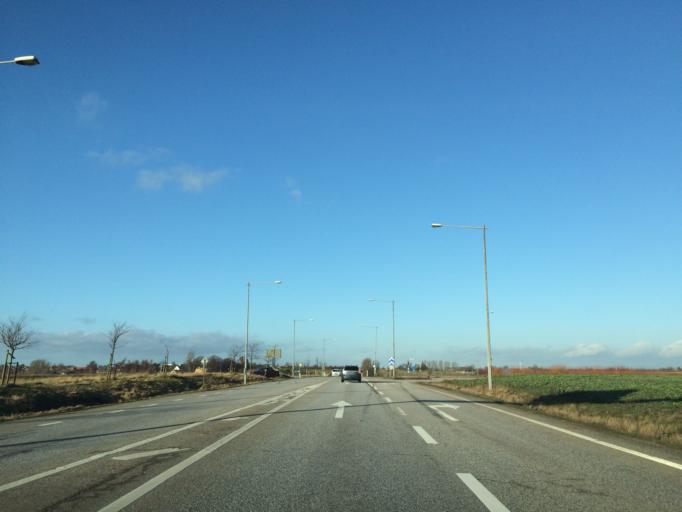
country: SE
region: Skane
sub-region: Kavlinge Kommun
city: Loddekopinge
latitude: 55.7481
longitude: 13.0282
